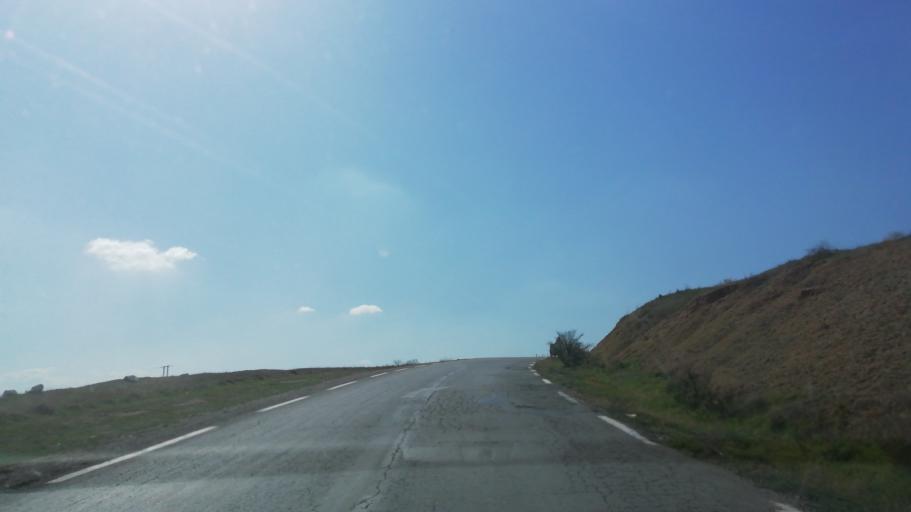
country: DZ
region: Mascara
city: Mascara
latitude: 35.5431
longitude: 0.1063
